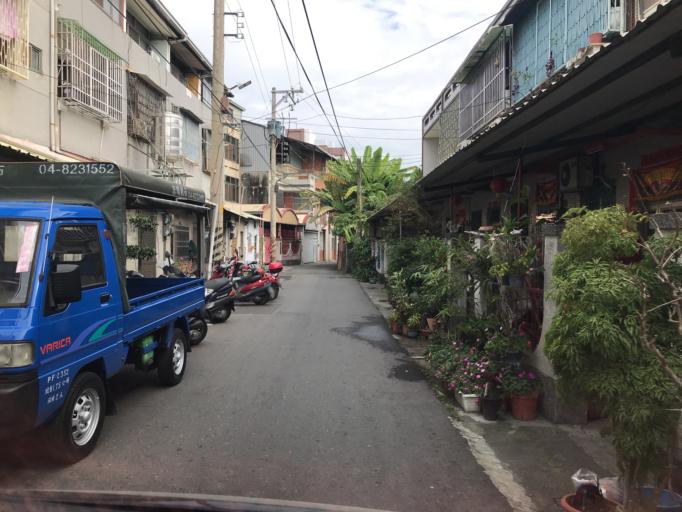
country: TW
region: Taiwan
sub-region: Nantou
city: Nantou
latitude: 23.8950
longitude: 120.5873
